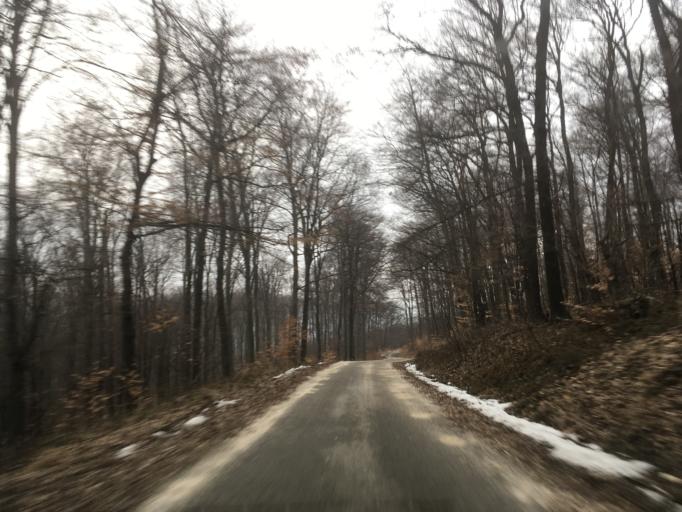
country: HU
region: Pest
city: Pilisszentkereszt
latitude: 47.7216
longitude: 18.8654
